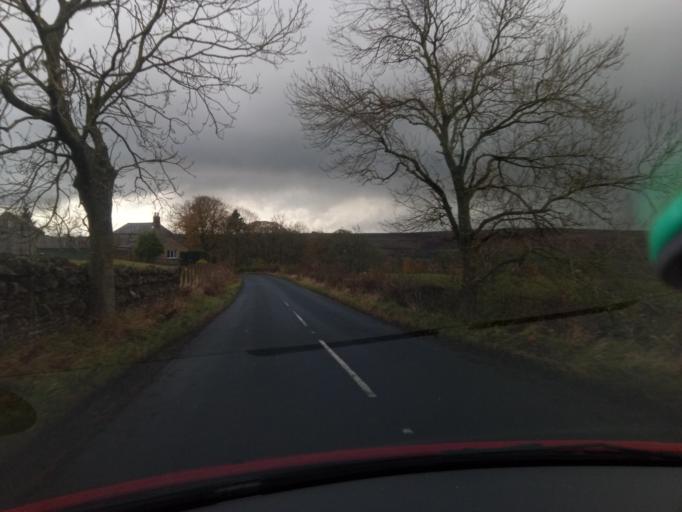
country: GB
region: England
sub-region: Northumberland
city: Corsenside
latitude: 55.1507
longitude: -2.2577
